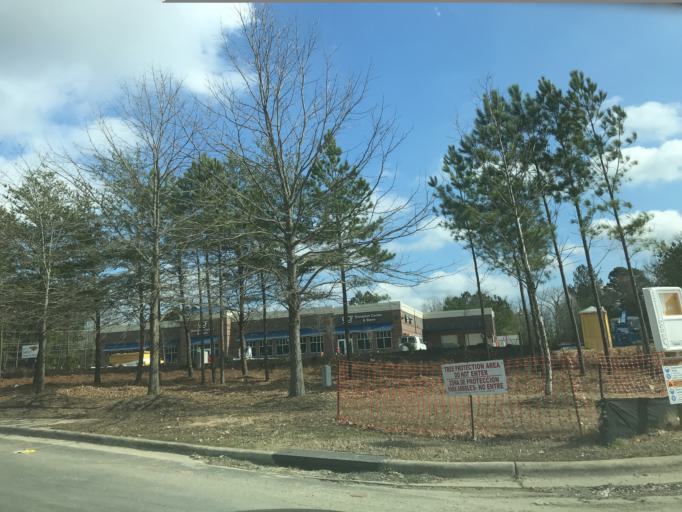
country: US
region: North Carolina
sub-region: Durham County
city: Gorman
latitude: 35.9757
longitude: -78.7917
